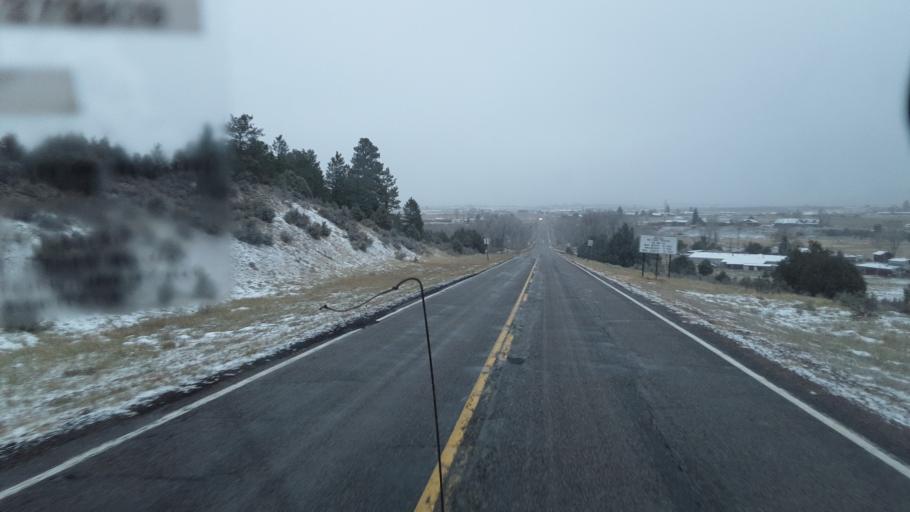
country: US
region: New Mexico
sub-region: Rio Arriba County
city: Tierra Amarilla
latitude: 36.6952
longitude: -106.5582
